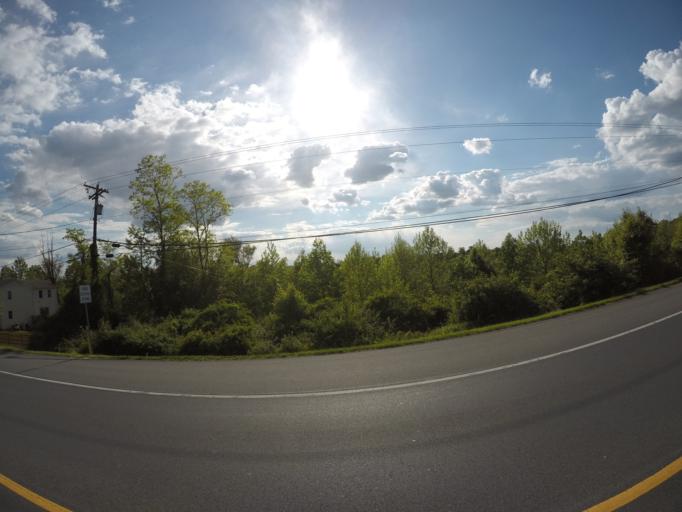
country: US
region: Maryland
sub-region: Montgomery County
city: Clarksburg
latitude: 39.2458
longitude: -77.2326
